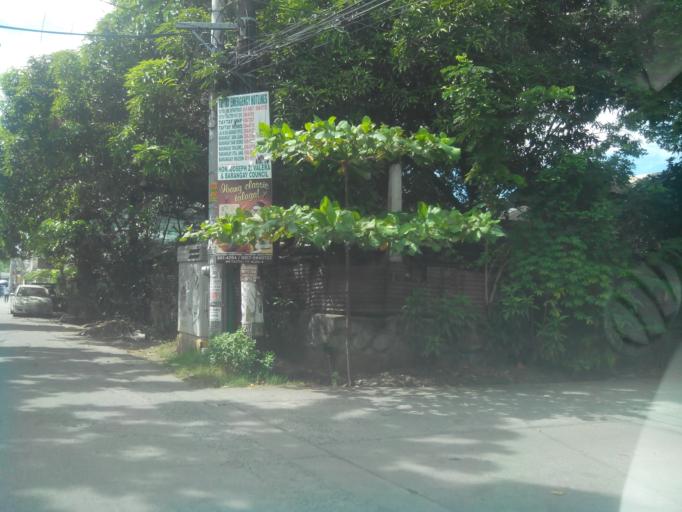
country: PH
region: Calabarzon
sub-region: Province of Rizal
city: Taytay
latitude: 14.5567
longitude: 121.1380
